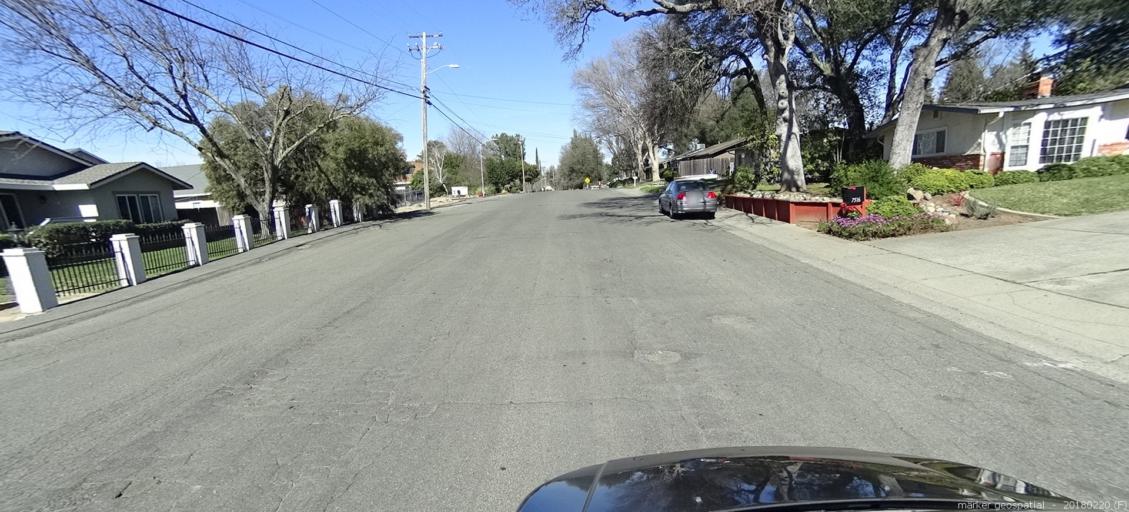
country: US
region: California
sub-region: Sacramento County
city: Orangevale
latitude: 38.7025
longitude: -121.2351
